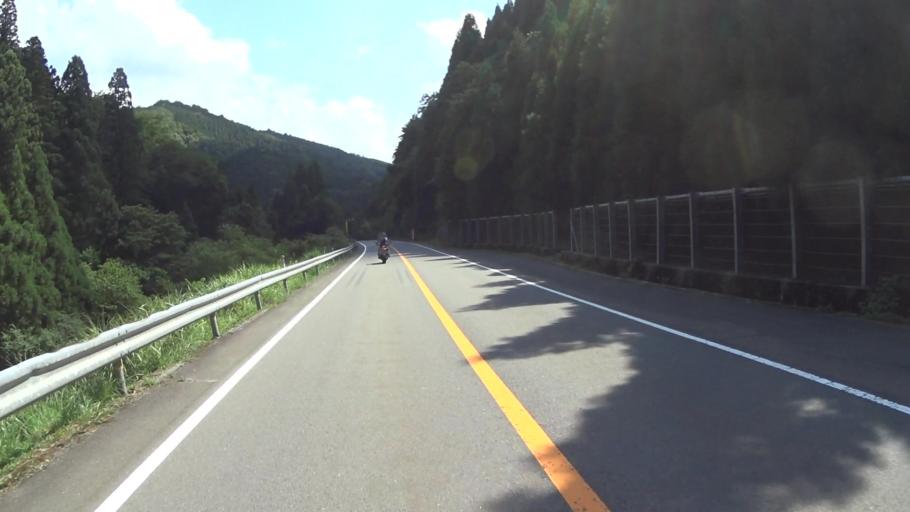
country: JP
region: Fukui
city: Obama
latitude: 35.3611
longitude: 135.5989
